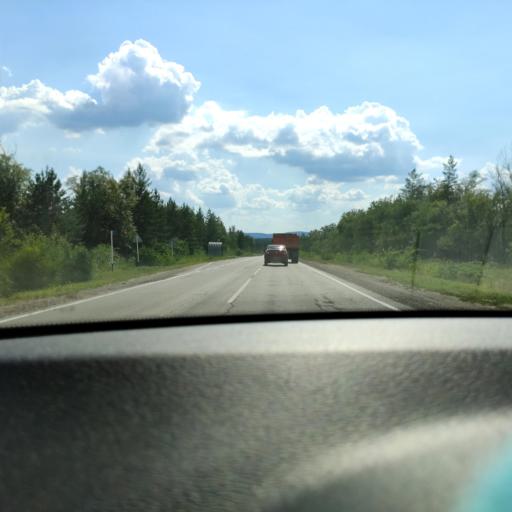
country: RU
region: Samara
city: Volzhskiy
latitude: 53.4588
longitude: 50.1699
